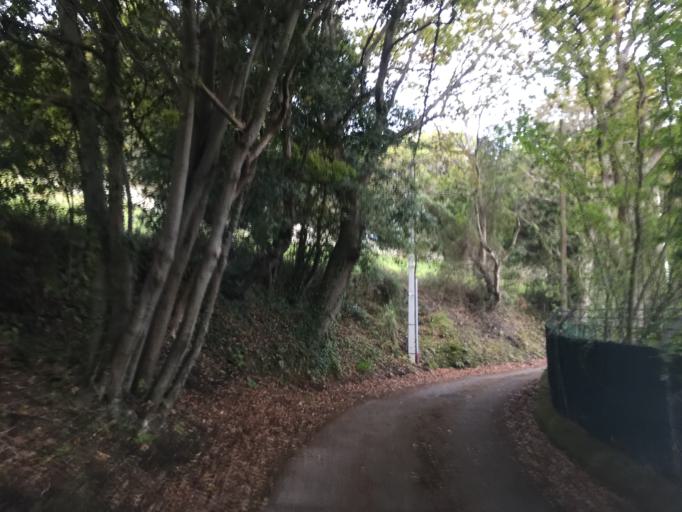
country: ES
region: Asturias
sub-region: Province of Asturias
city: Gijon
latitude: 43.5446
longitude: -5.6207
